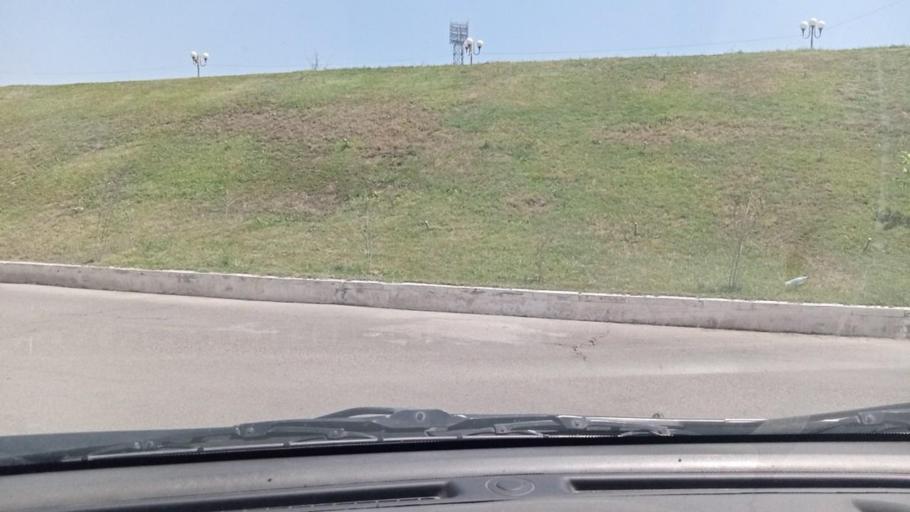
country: UZ
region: Toshkent Shahri
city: Tashkent
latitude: 41.2746
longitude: 69.2802
